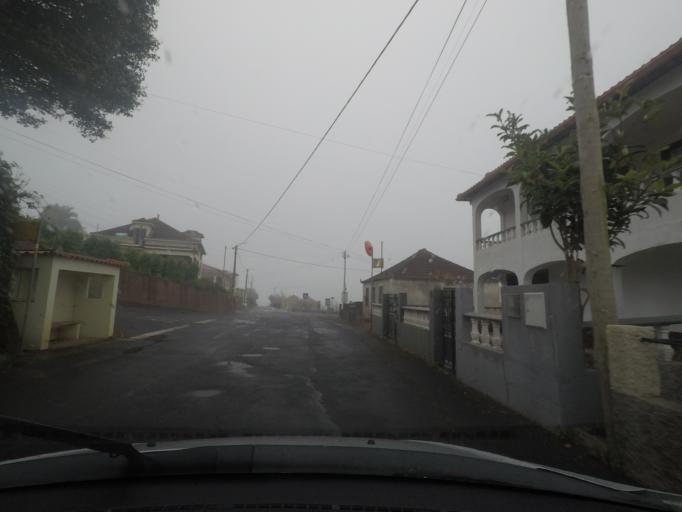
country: PT
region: Madeira
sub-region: Santana
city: Santana
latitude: 32.7976
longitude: -16.8771
